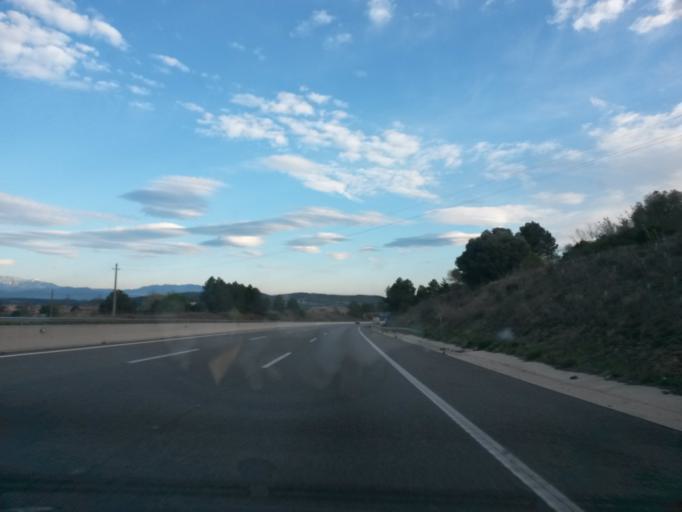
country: ES
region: Catalonia
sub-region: Provincia de Girona
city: Bascara
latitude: 42.1525
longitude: 2.9174
